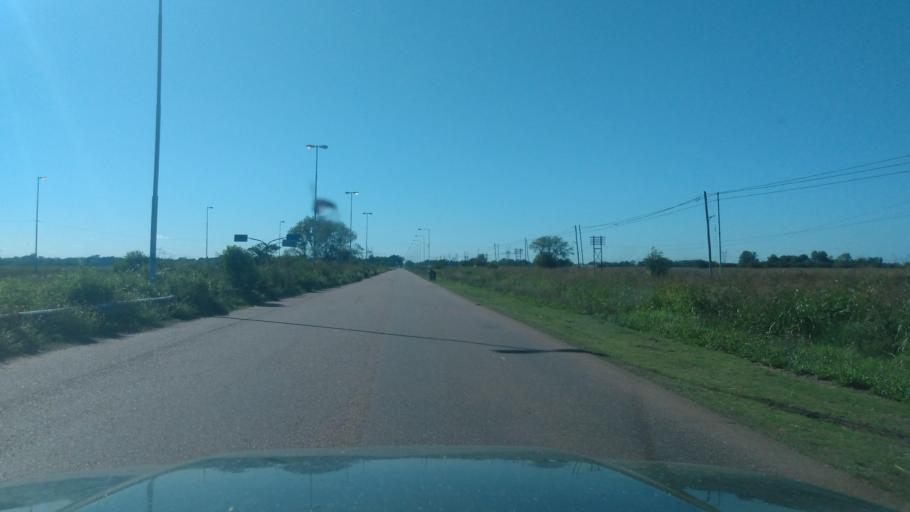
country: AR
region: Buenos Aires
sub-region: Partido de Lujan
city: Lujan
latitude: -34.5891
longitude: -59.0360
